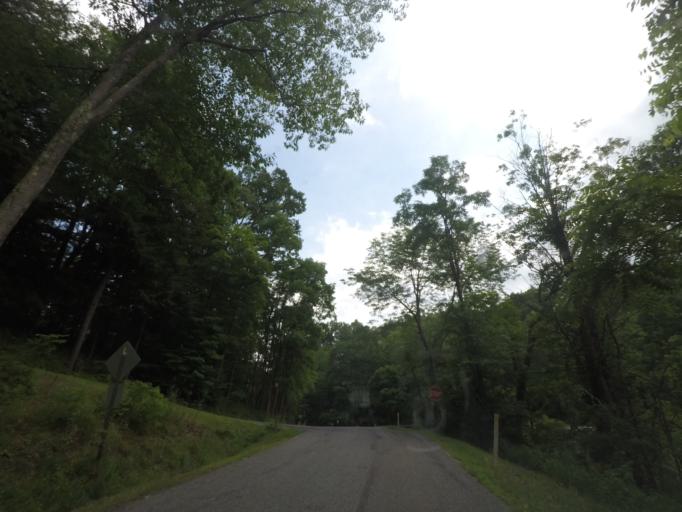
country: US
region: New York
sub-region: Saratoga County
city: Stillwater
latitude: 43.0077
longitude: -73.6190
